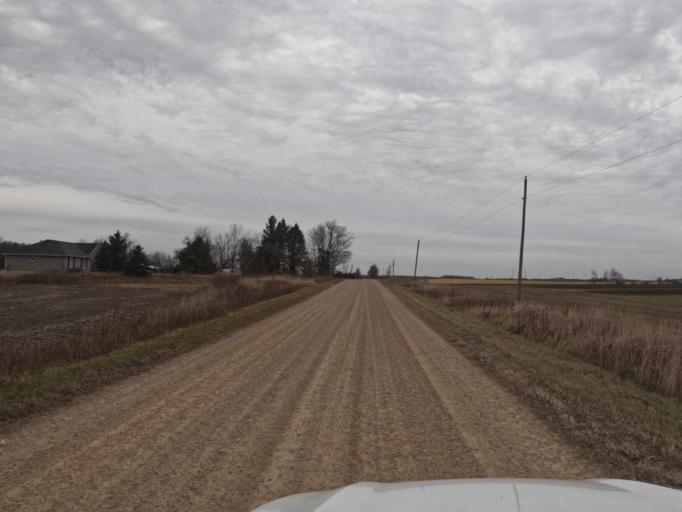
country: CA
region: Ontario
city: Shelburne
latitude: 44.0249
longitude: -80.3699
